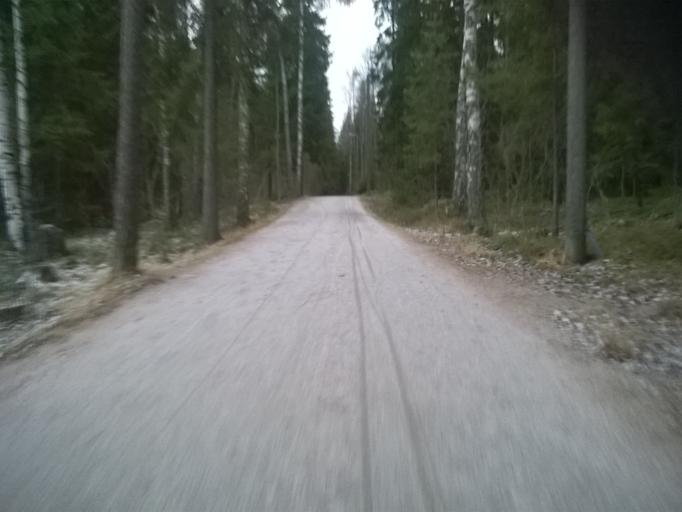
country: FI
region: Uusimaa
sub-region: Helsinki
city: Helsinki
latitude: 60.2506
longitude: 24.9090
